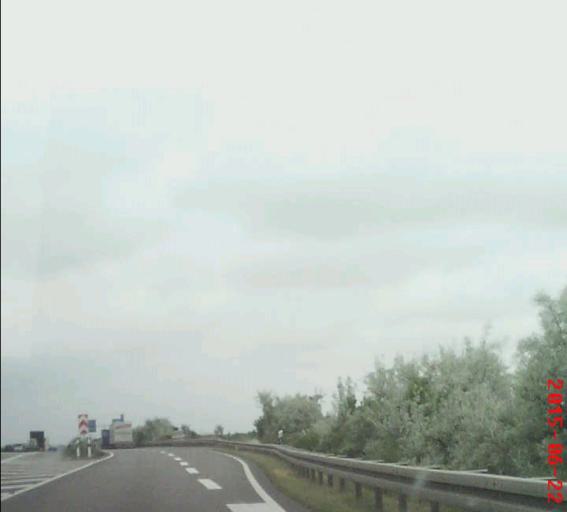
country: DE
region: Saxony-Anhalt
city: Peissen
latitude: 51.5007
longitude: 12.0506
